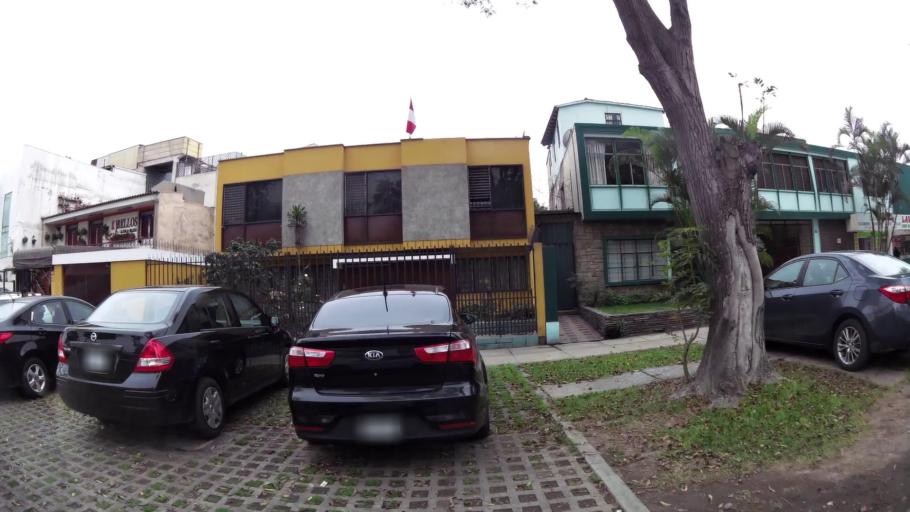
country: PE
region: Lima
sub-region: Lima
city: Surco
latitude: -12.1228
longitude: -77.0182
